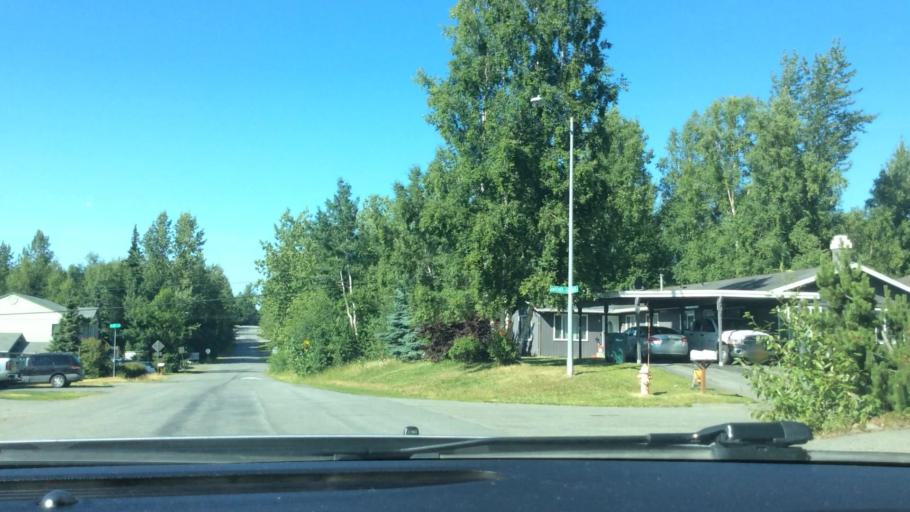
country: US
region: Alaska
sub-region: Anchorage Municipality
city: Anchorage
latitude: 61.1974
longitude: -149.7859
